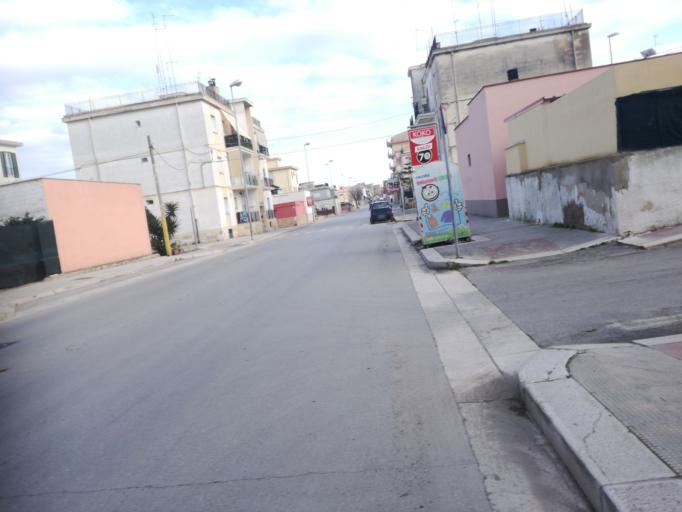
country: IT
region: Apulia
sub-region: Provincia di Barletta - Andria - Trani
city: Andria
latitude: 41.2398
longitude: 16.2959
